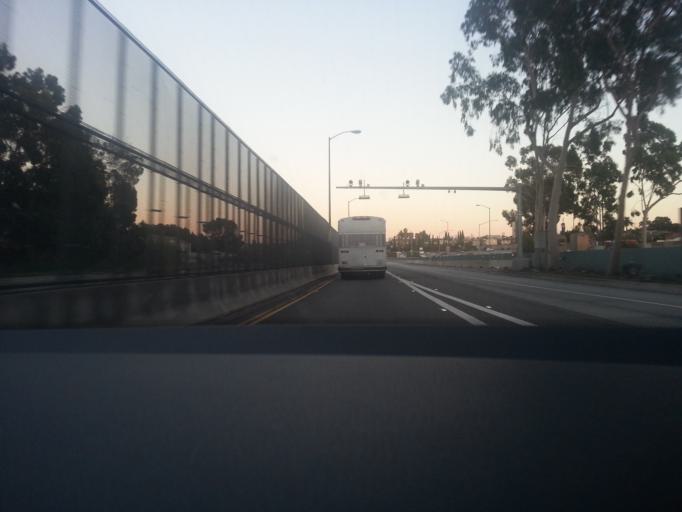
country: US
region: California
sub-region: Los Angeles County
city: Boyle Heights
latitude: 34.0555
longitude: -118.2104
